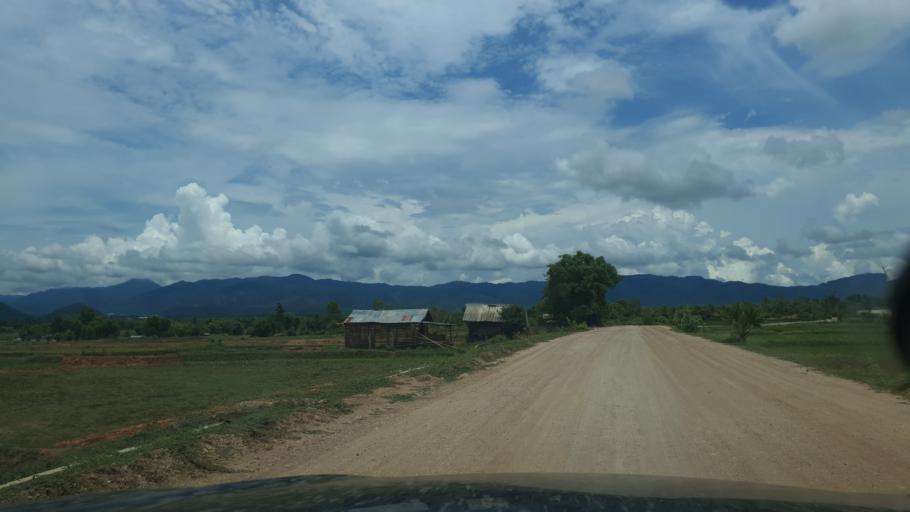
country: TH
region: Lampang
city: Sop Prap
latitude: 17.9380
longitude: 99.3611
